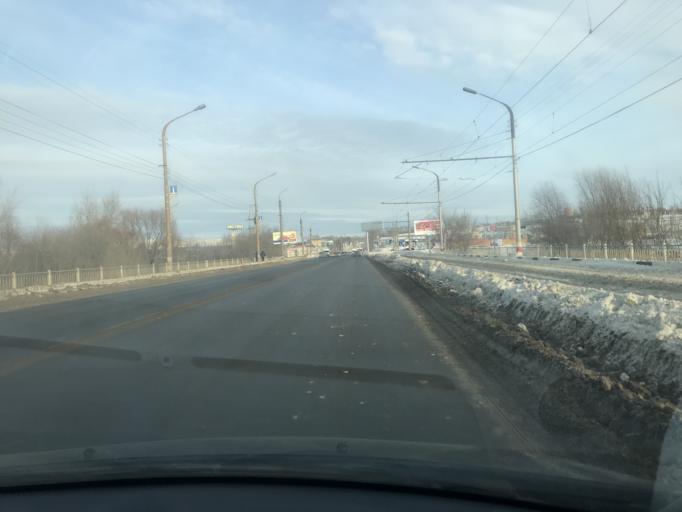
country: RU
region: Ulyanovsk
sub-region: Ulyanovskiy Rayon
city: Ulyanovsk
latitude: 54.3249
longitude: 48.3572
